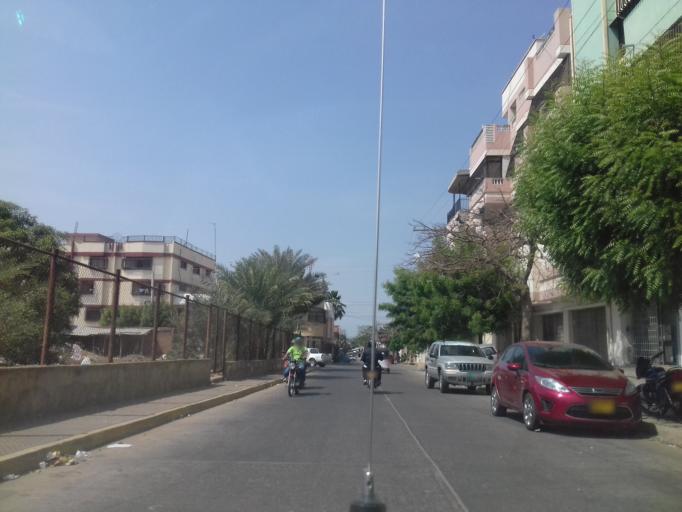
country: CO
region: La Guajira
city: Maicao
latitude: 11.3785
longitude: -72.2355
